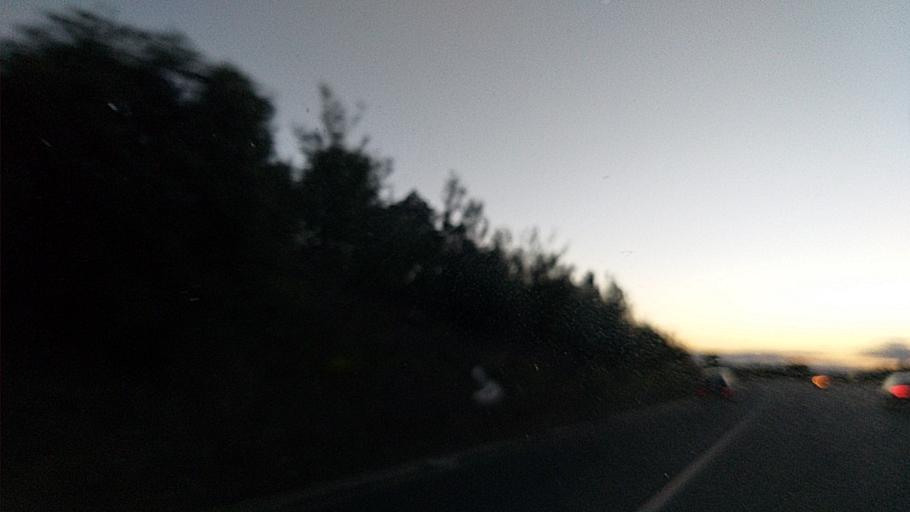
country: AU
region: New South Wales
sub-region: Campbelltown Municipality
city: Denham Court
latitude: -33.9813
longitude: 150.8644
